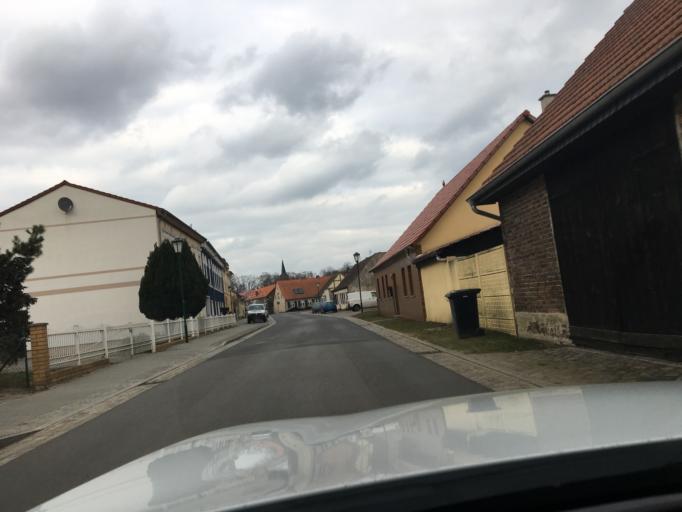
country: DE
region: Brandenburg
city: Liebenwalde
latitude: 52.8789
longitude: 13.4386
